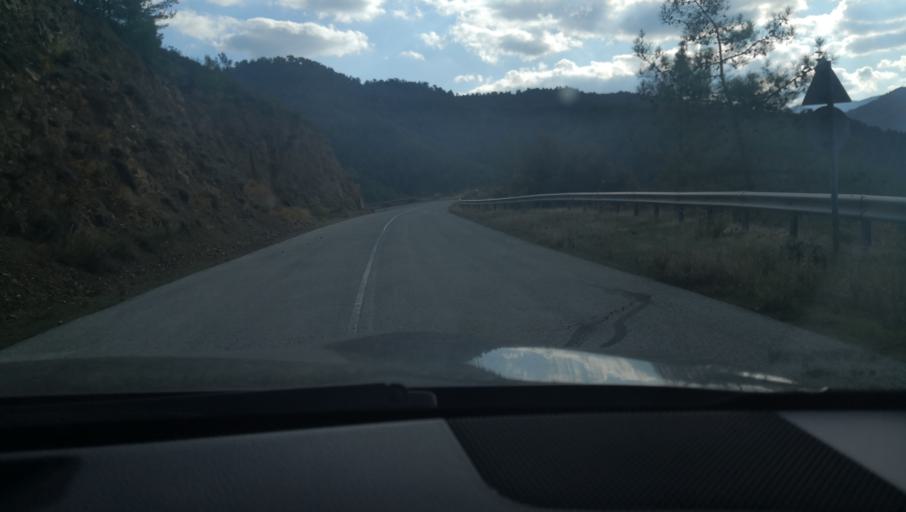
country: CY
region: Lefkosia
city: Lefka
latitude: 35.0576
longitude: 32.7486
